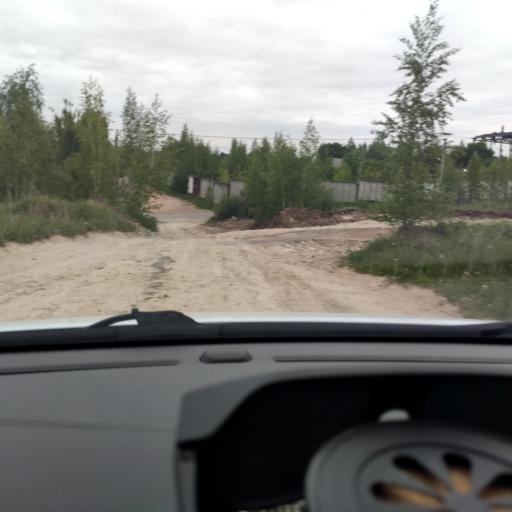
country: RU
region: Tatarstan
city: Vysokaya Gora
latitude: 55.8574
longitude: 49.2511
